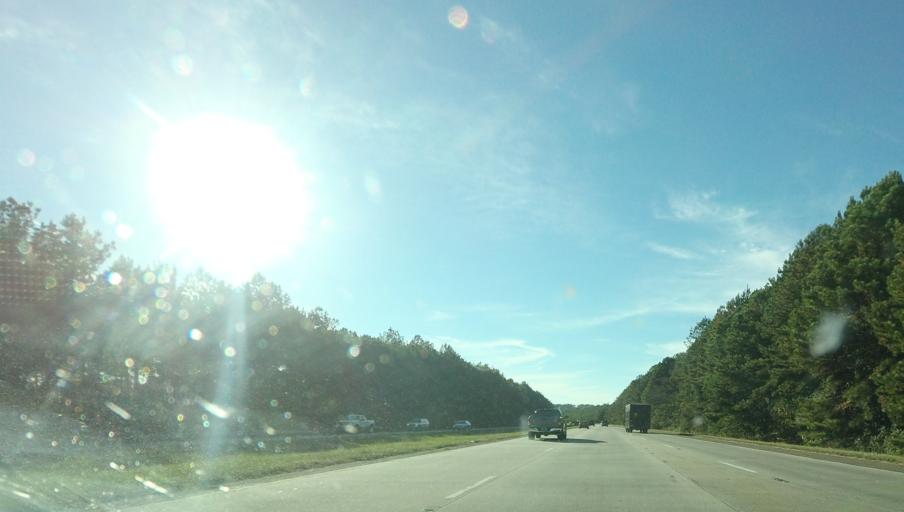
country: US
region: Georgia
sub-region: Muscogee County
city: Columbus
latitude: 32.5548
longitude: -84.9123
